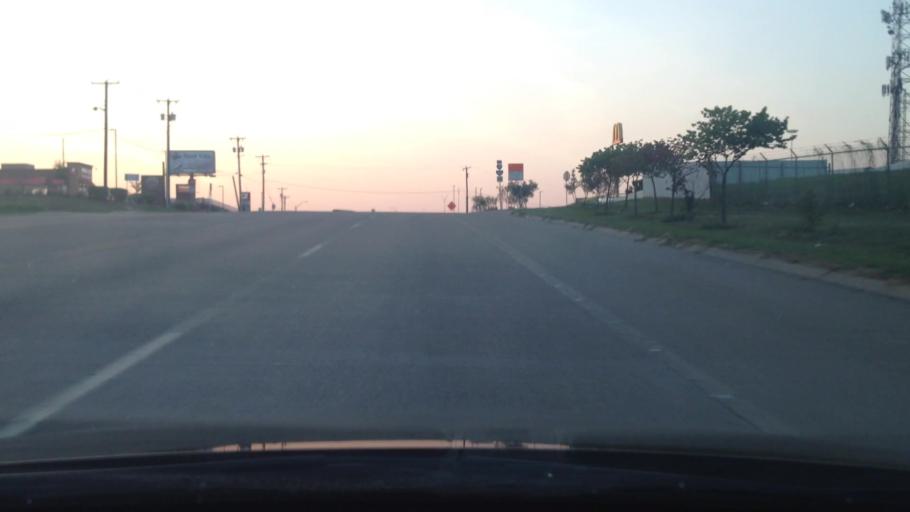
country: US
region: Texas
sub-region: Tarrant County
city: Kennedale
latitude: 32.6632
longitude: -97.2388
